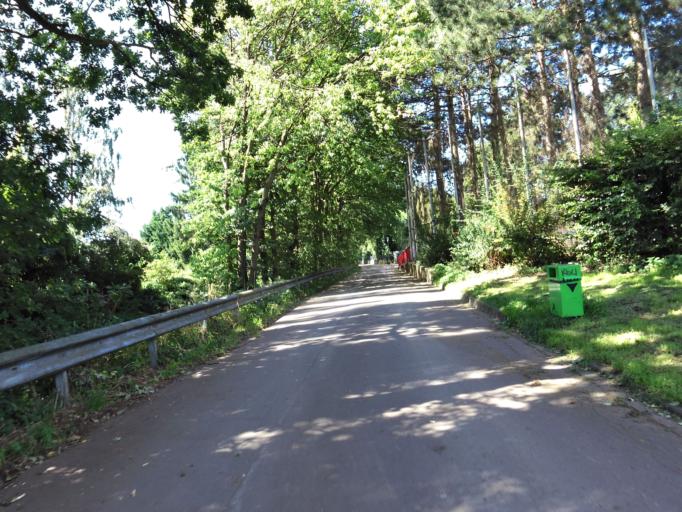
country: DE
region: North Rhine-Westphalia
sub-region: Regierungsbezirk Koln
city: Herzogenrath
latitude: 50.8875
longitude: 6.1078
